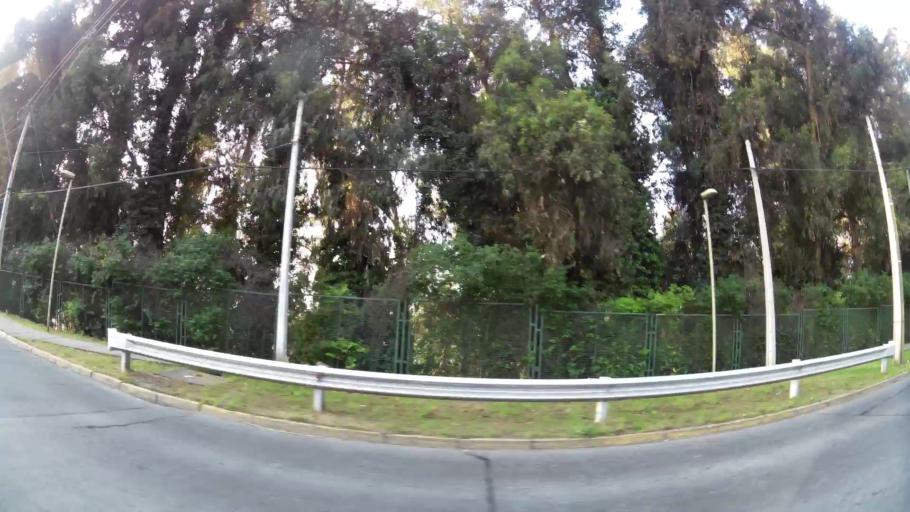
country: CL
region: Santiago Metropolitan
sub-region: Provincia de Santiago
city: Villa Presidente Frei, Nunoa, Santiago, Chile
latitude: -33.3928
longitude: -70.5335
